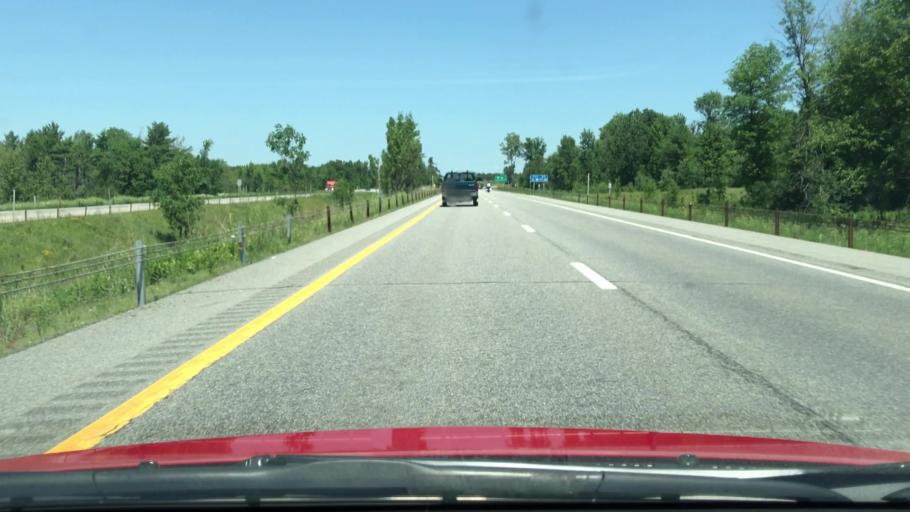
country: US
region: New York
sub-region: Essex County
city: Keeseville
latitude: 44.4352
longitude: -73.4916
